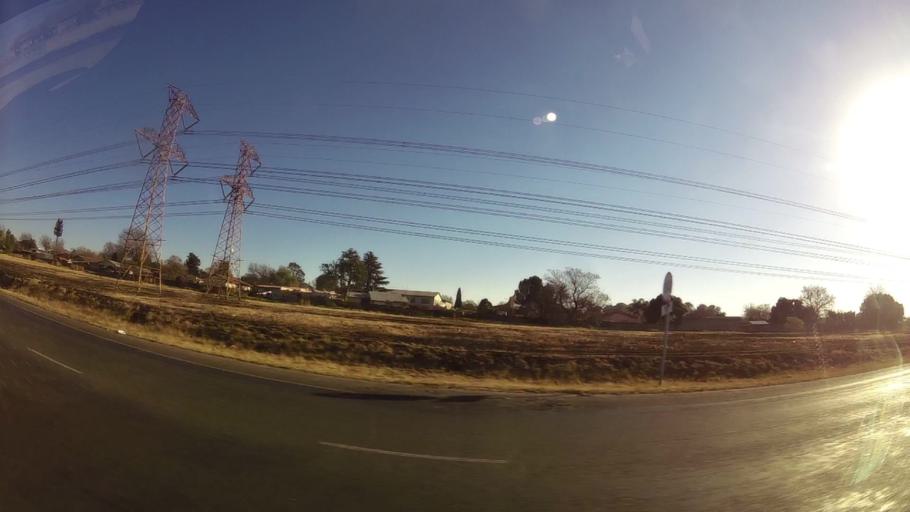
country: ZA
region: Gauteng
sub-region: City of Johannesburg Metropolitan Municipality
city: Modderfontein
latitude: -26.0887
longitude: 28.1945
